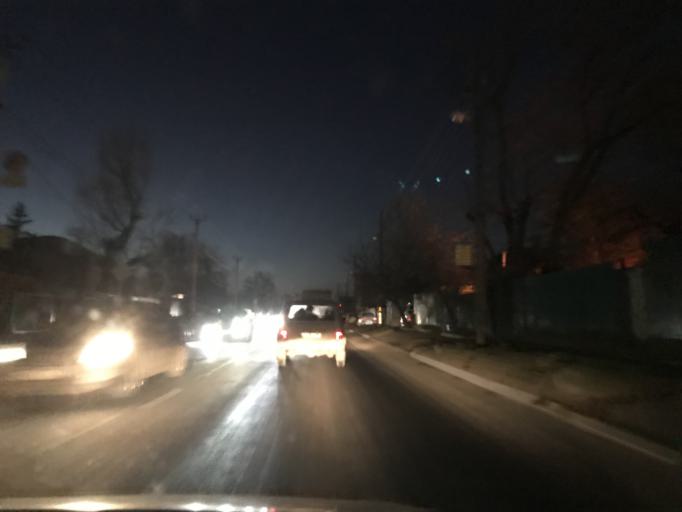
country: RU
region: Rostov
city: Rostov-na-Donu
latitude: 47.1917
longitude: 39.6222
